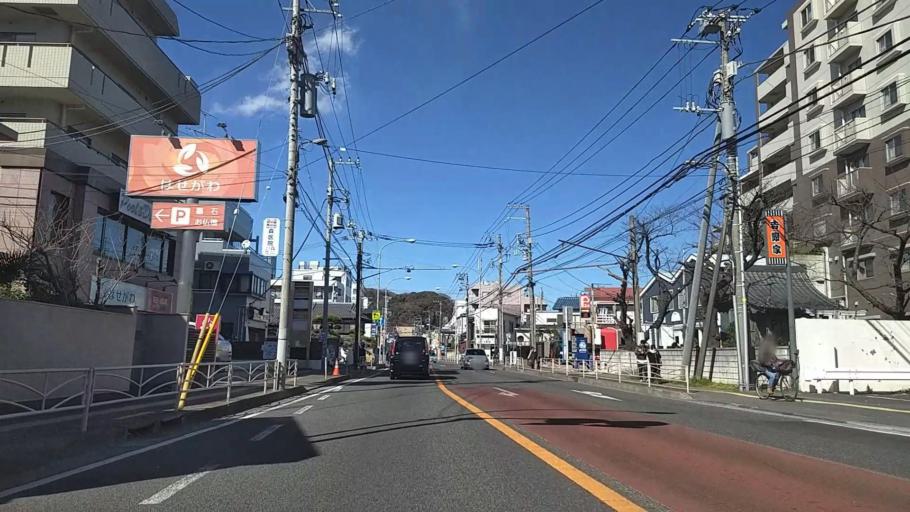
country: JP
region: Kanagawa
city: Zushi
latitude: 35.3418
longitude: 139.6235
